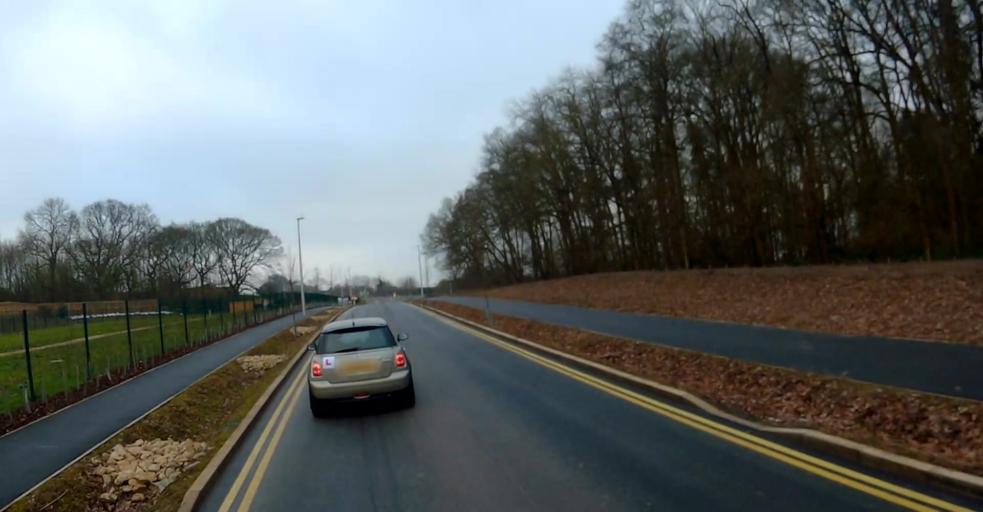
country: GB
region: England
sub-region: Wokingham
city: Wokingham
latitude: 51.4188
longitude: -0.8110
